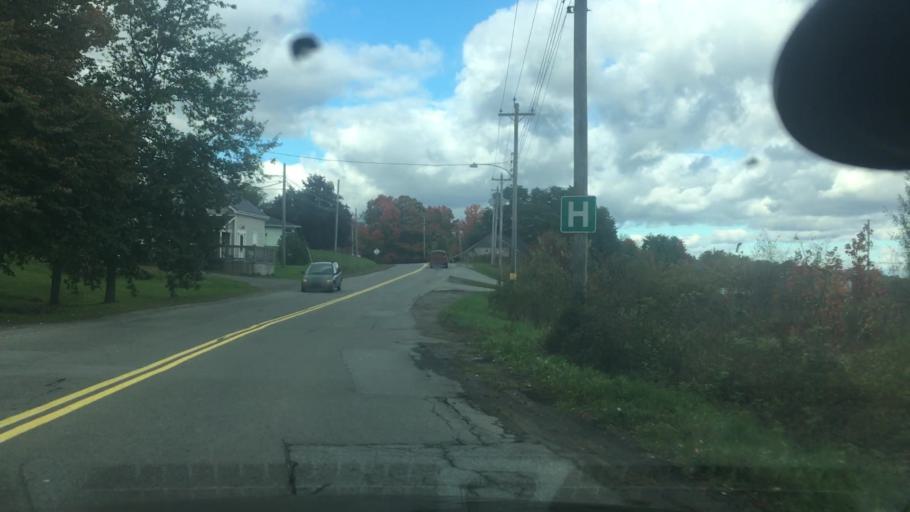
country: CA
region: Nova Scotia
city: Windsor
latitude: 44.9769
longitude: -64.1213
